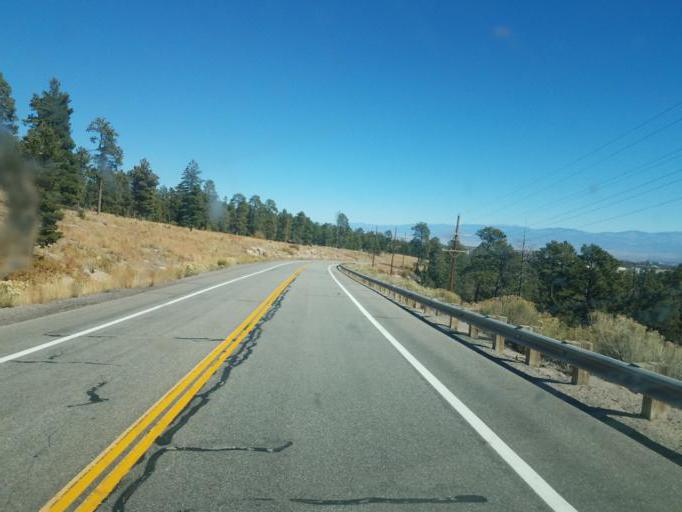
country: US
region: New Mexico
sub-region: Los Alamos County
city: Los Alamos
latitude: 35.8735
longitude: -106.3422
